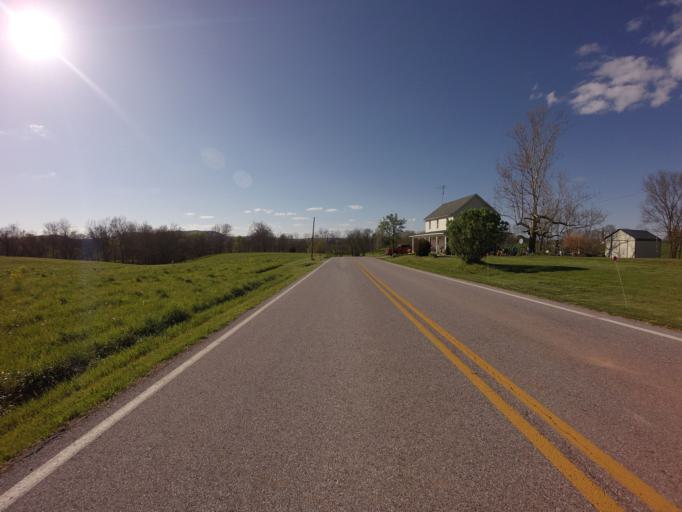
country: US
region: Maryland
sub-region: Frederick County
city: Emmitsburg
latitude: 39.6701
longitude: -77.2973
